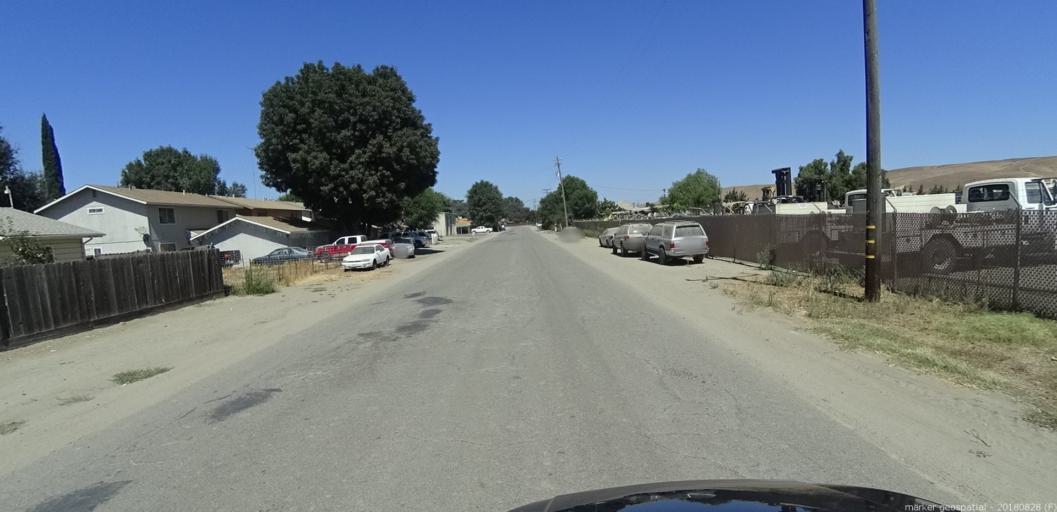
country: US
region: California
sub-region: San Luis Obispo County
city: Lake Nacimiento
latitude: 36.0208
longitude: -120.9025
